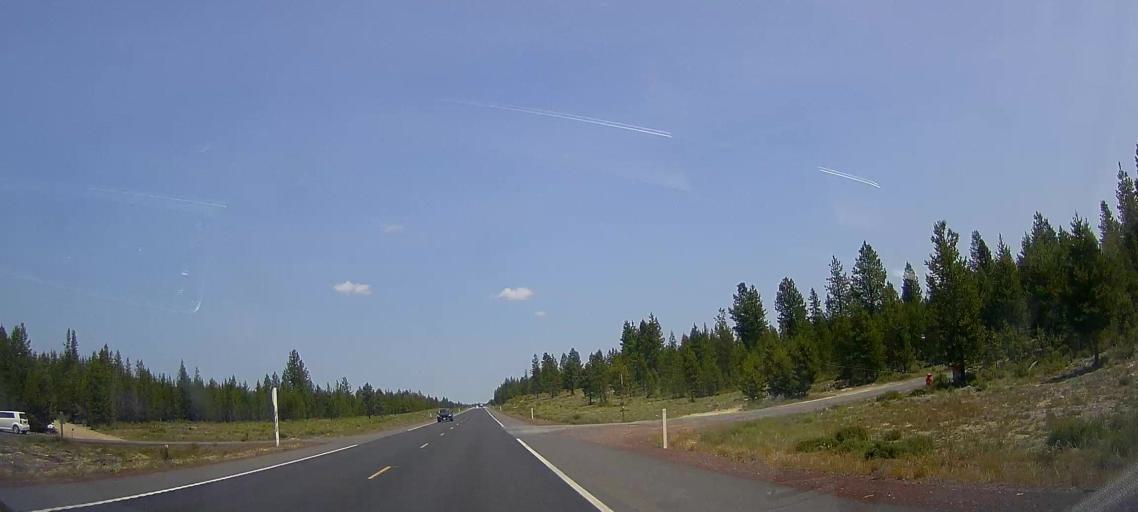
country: US
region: Oregon
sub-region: Deschutes County
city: La Pine
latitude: 43.5068
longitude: -121.6623
